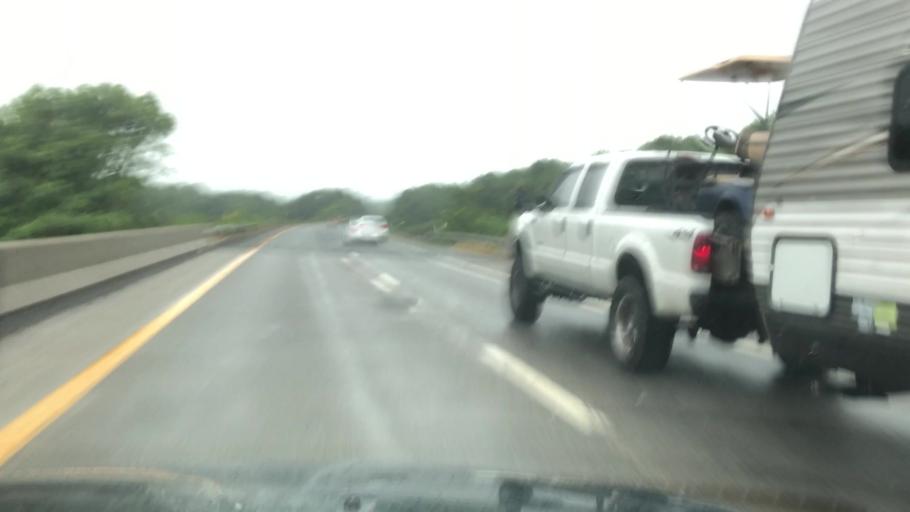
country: US
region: New York
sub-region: Orange County
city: Otisville
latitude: 41.3936
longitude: -74.5552
